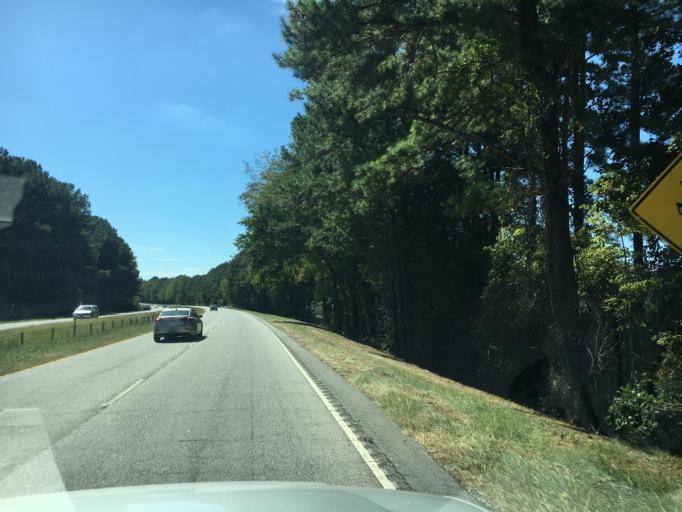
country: US
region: South Carolina
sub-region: Pickens County
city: Liberty
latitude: 34.7501
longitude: -82.7092
